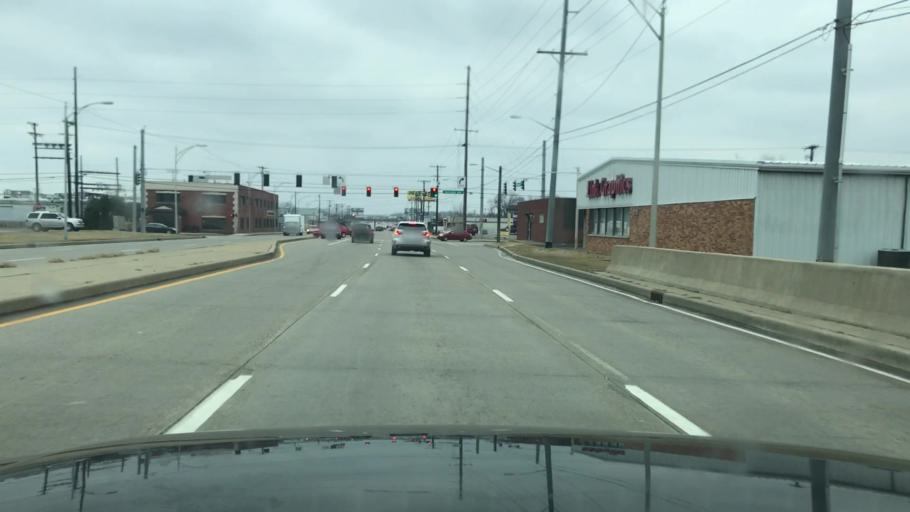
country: US
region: Indiana
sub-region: Vanderburgh County
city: Evansville
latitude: 37.9993
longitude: -87.5461
